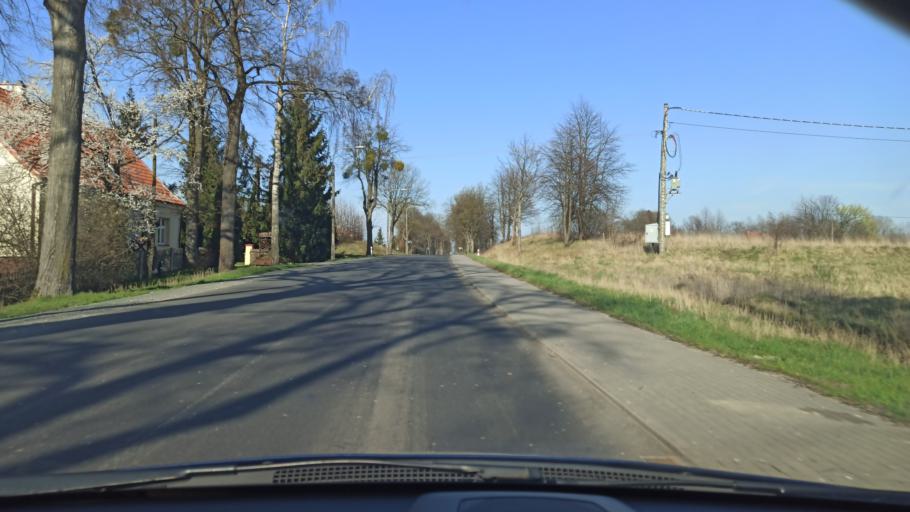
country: PL
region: Warmian-Masurian Voivodeship
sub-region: Powiat elblaski
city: Gronowo Gorne
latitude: 54.2105
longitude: 19.5103
